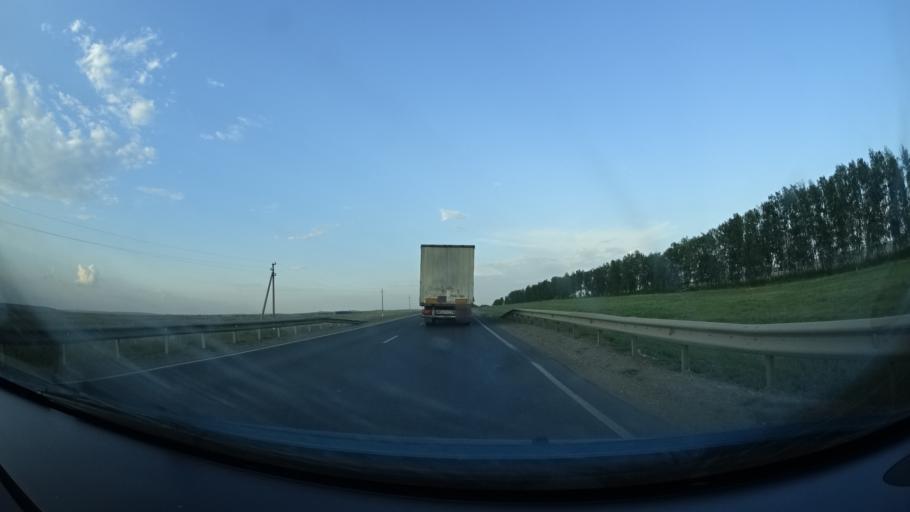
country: RU
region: Samara
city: Kamyshla
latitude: 54.0525
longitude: 52.0466
